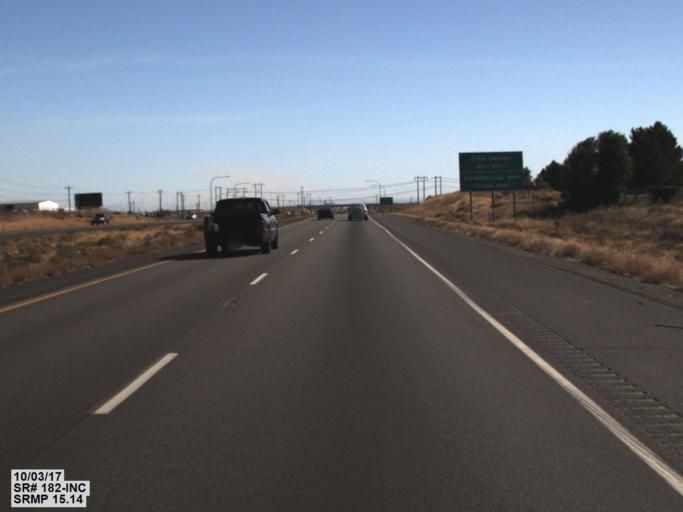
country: US
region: Washington
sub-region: Franklin County
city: Pasco
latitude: 46.2473
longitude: -119.0685
